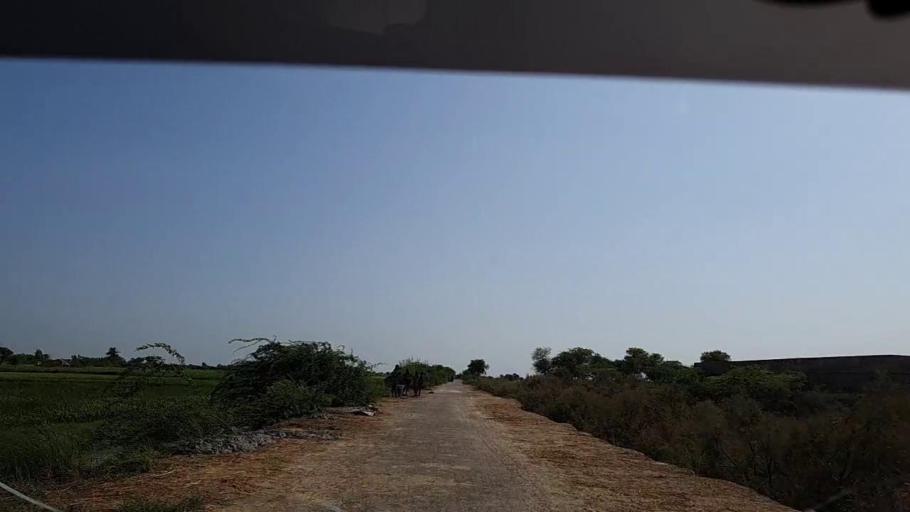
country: PK
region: Sindh
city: Badin
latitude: 24.6312
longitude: 68.7834
